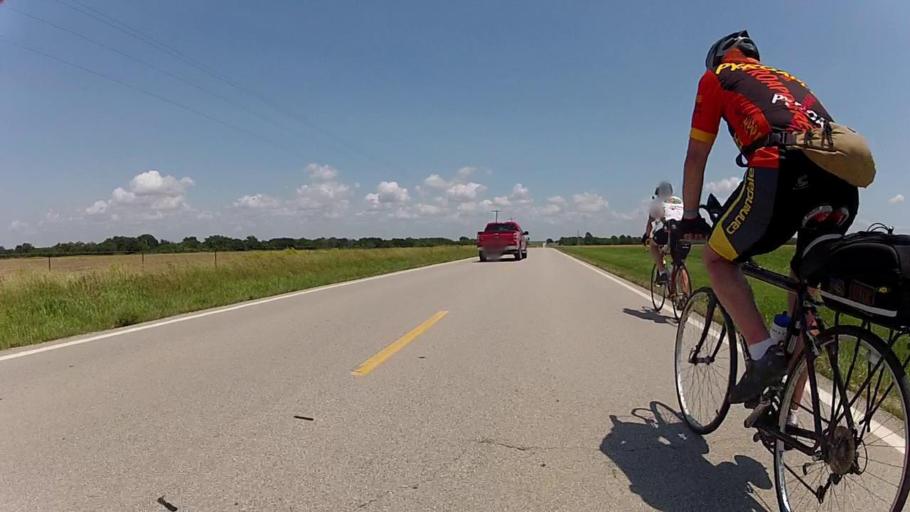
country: US
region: Kansas
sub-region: Montgomery County
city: Cherryvale
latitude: 37.1929
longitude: -95.4577
